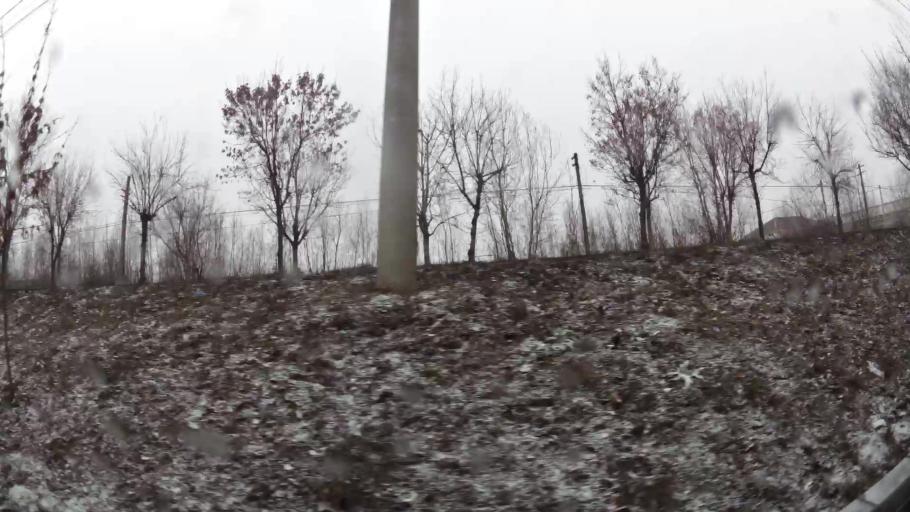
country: RO
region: Dambovita
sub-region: Municipiul Targoviste
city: Targoviste
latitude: 44.9104
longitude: 25.4568
